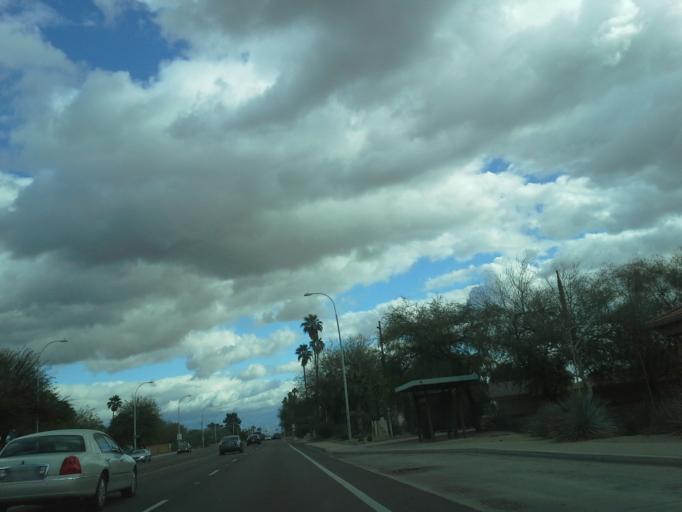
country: US
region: Arizona
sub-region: Maricopa County
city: Scottsdale
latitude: 33.4803
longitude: -111.9063
